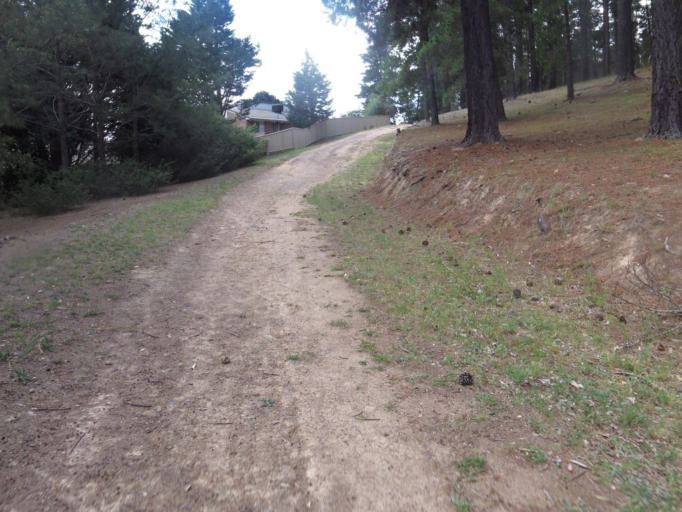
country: AU
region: Australian Capital Territory
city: Macarthur
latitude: -35.3744
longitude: 149.1185
